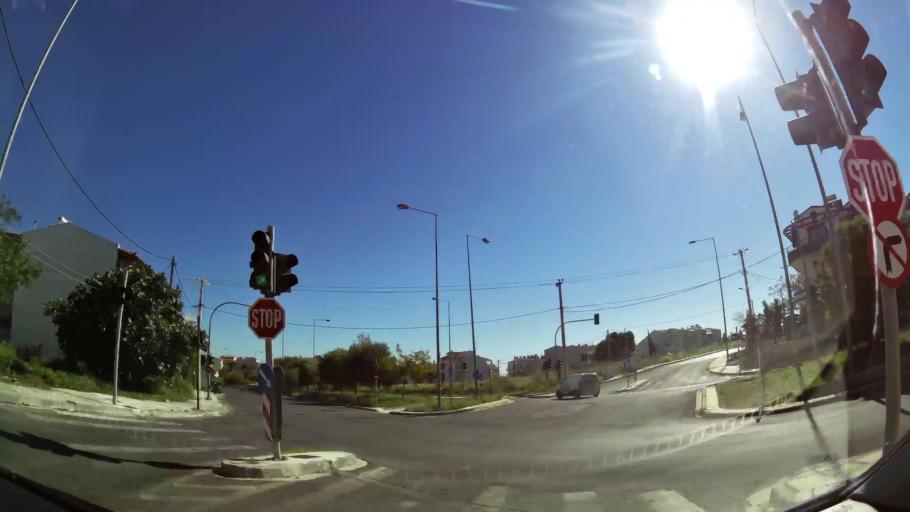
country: GR
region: Attica
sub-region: Nomarchia Anatolikis Attikis
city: Leondarion
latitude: 37.9995
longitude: 23.8523
